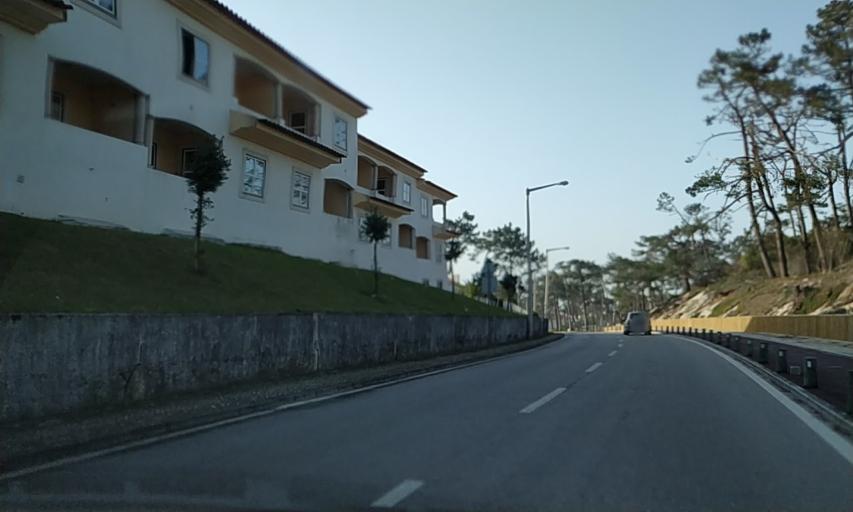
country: PT
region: Leiria
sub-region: Alcobaca
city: Pataias
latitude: 39.7560
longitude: -9.0259
